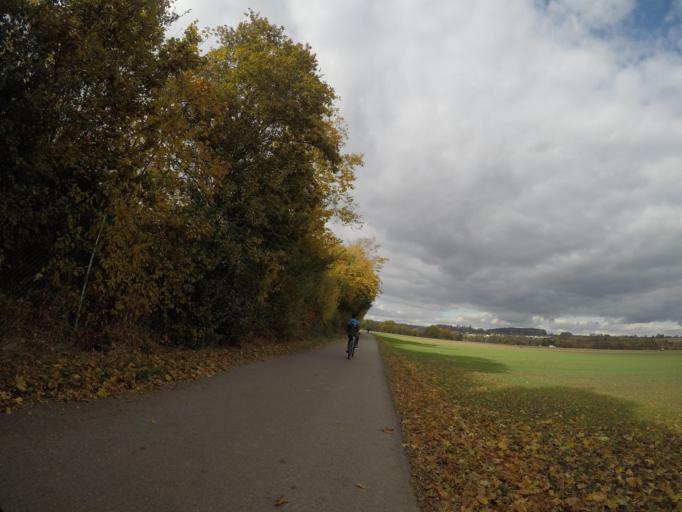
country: DE
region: Baden-Wuerttemberg
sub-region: Tuebingen Region
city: Emerkingen
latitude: 48.2259
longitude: 9.6555
